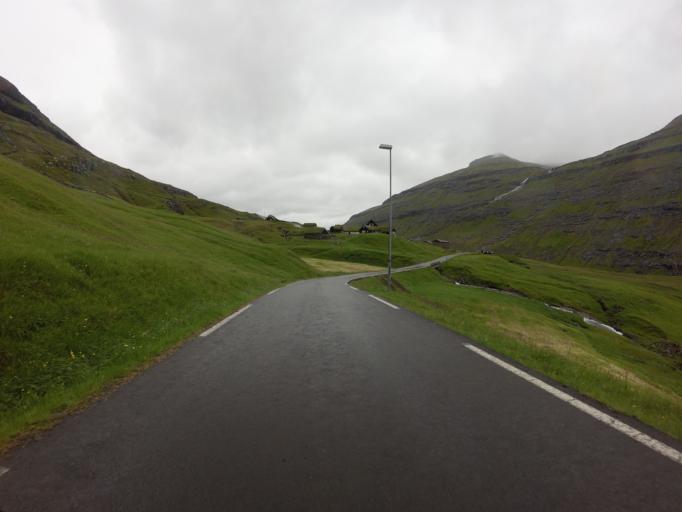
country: FO
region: Streymoy
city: Vestmanna
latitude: 62.2477
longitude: -7.1780
